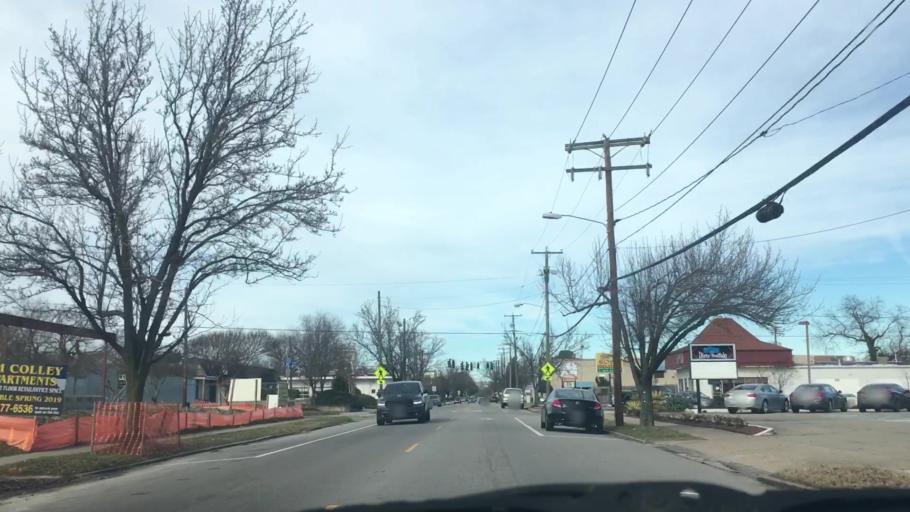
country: US
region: Virginia
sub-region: City of Norfolk
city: Norfolk
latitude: 36.8817
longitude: -76.2947
